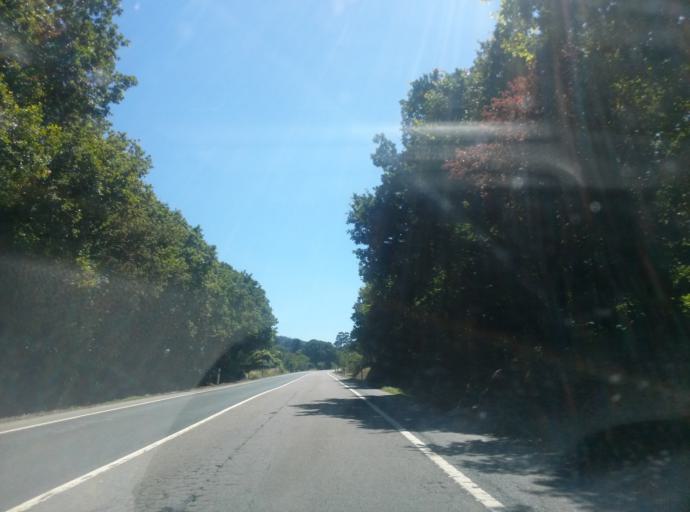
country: ES
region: Galicia
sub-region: Provincia de Lugo
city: Castro de Rei
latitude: 43.1670
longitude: -7.3762
